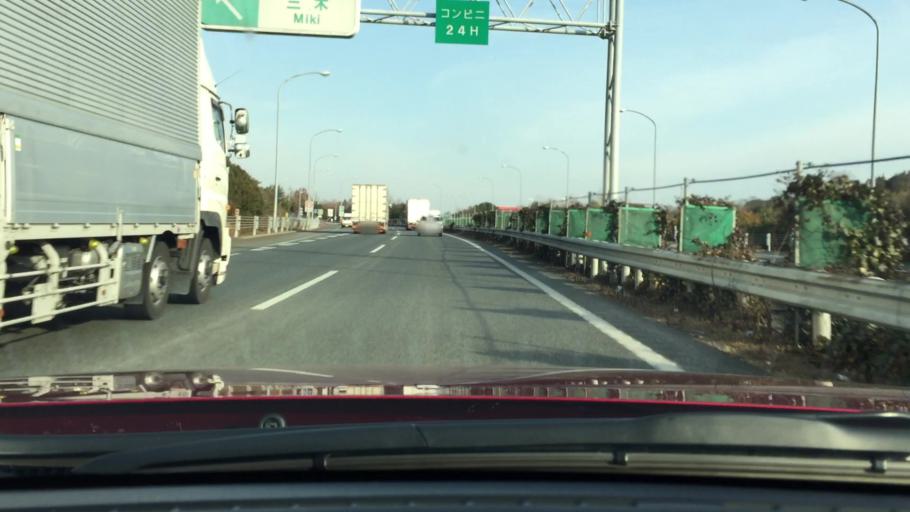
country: JP
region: Hyogo
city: Miki
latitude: 34.8164
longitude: 134.9755
